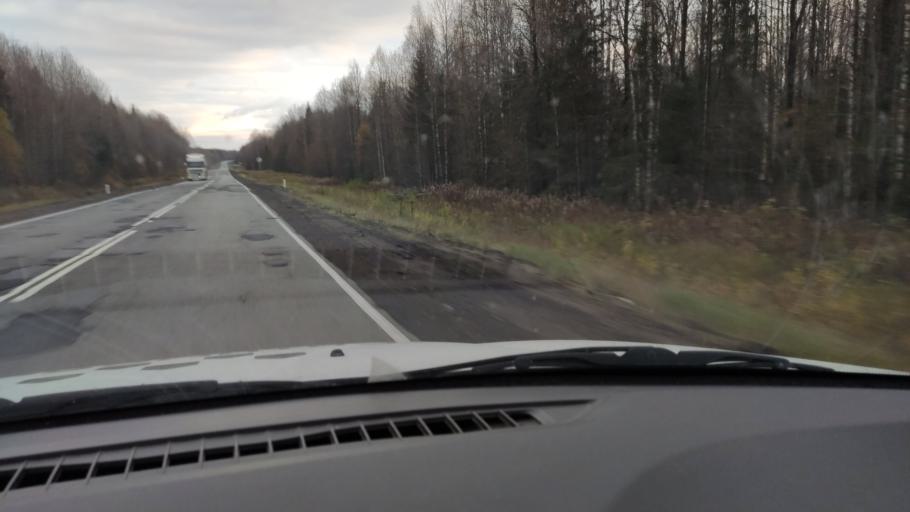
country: RU
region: Kirov
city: Omutninsk
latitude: 58.7577
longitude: 52.0259
